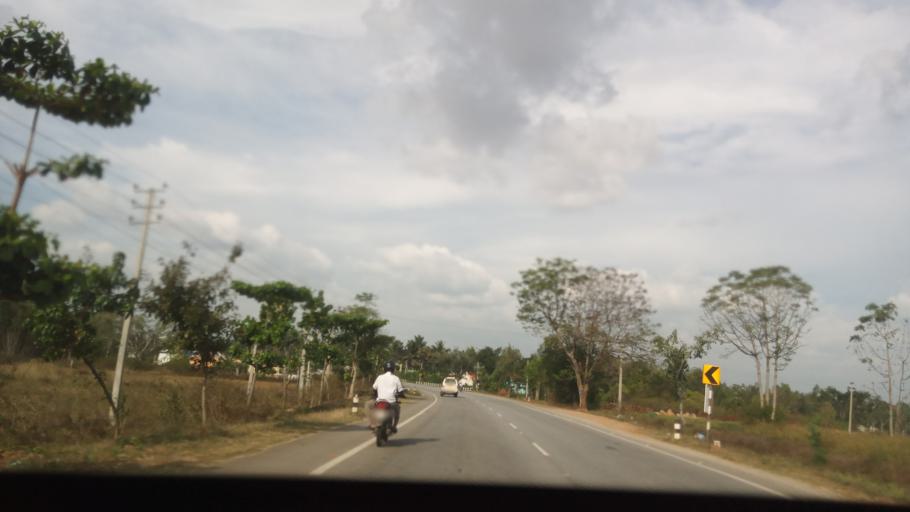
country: IN
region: Karnataka
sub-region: Mandya
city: Maddur
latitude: 12.6770
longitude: 77.0583
